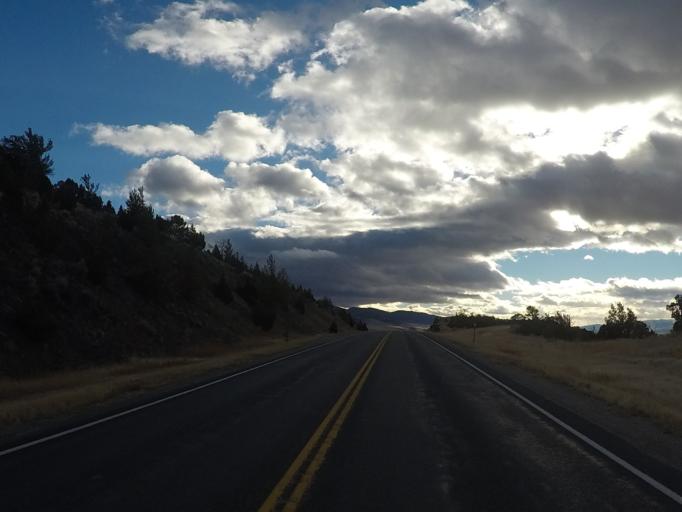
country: US
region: Montana
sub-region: Jefferson County
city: Whitehall
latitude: 45.8917
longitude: -111.9646
